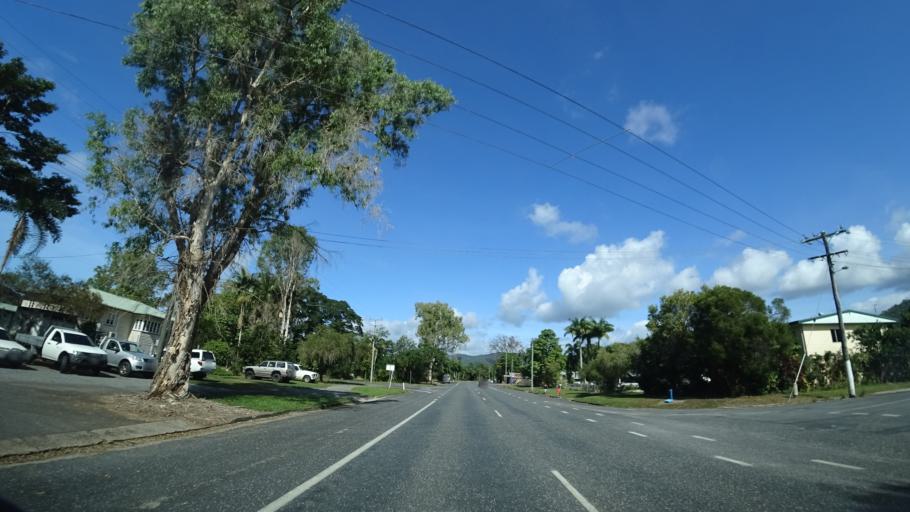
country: AU
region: Queensland
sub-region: Cairns
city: Port Douglas
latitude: -16.4780
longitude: 145.3760
